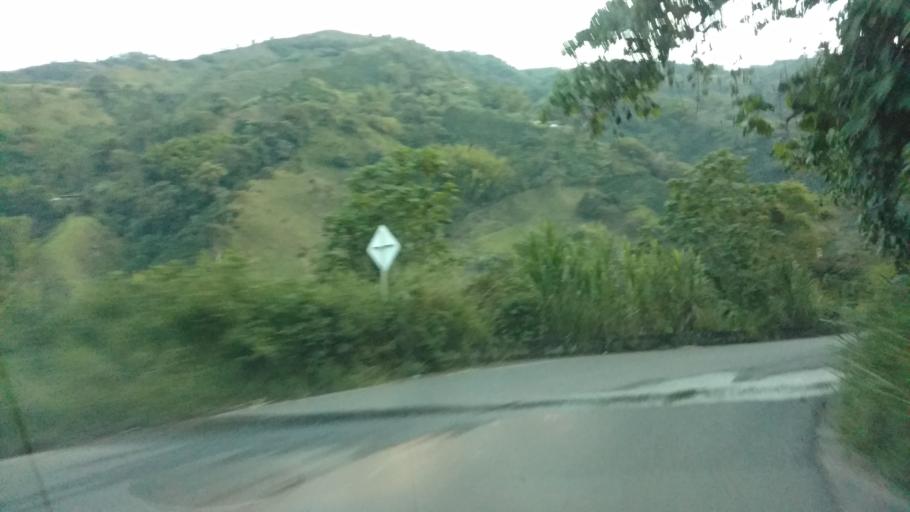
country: CO
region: Caldas
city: Aranzazu
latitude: 5.2561
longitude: -75.4992
